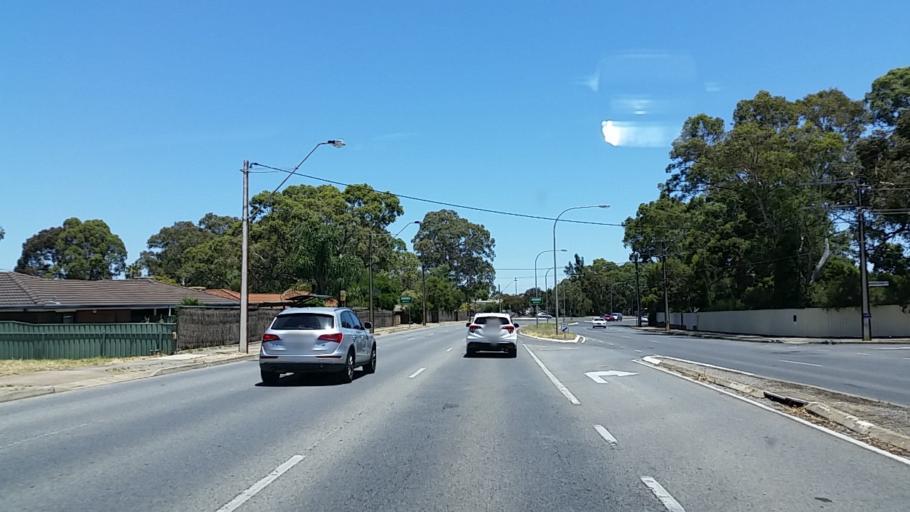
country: AU
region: South Australia
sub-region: Tea Tree Gully
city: Hope Valley
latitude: -34.8258
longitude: 138.7078
